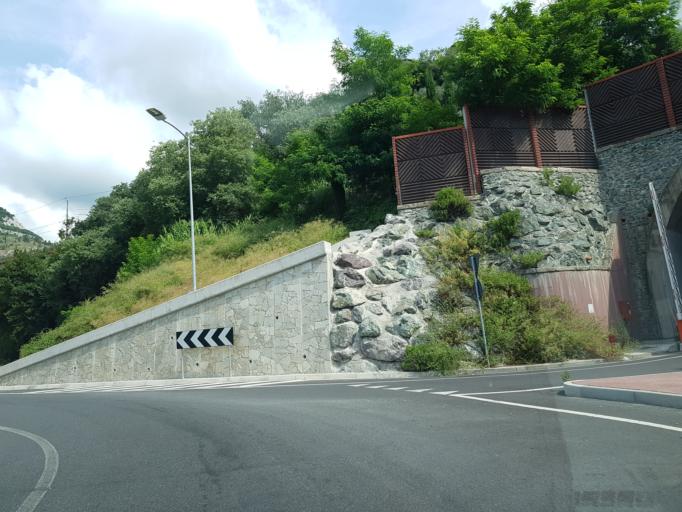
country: IT
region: Liguria
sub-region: Provincia di Genova
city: San Teodoro
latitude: 44.4337
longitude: 8.8613
